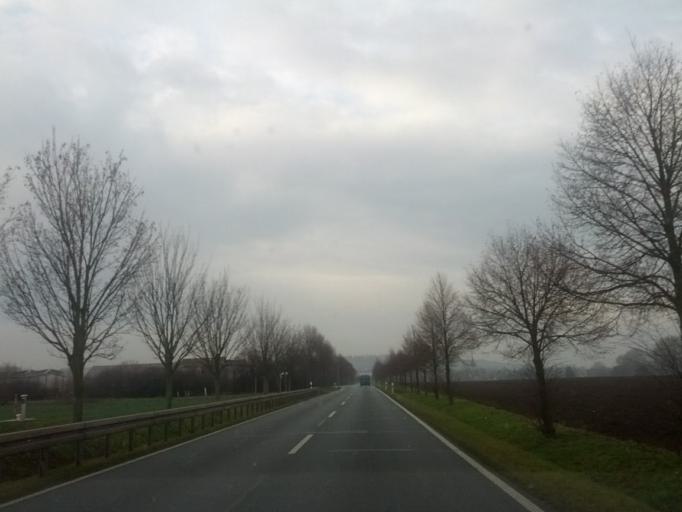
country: DE
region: Thuringia
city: Warza
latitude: 50.9941
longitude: 10.6758
